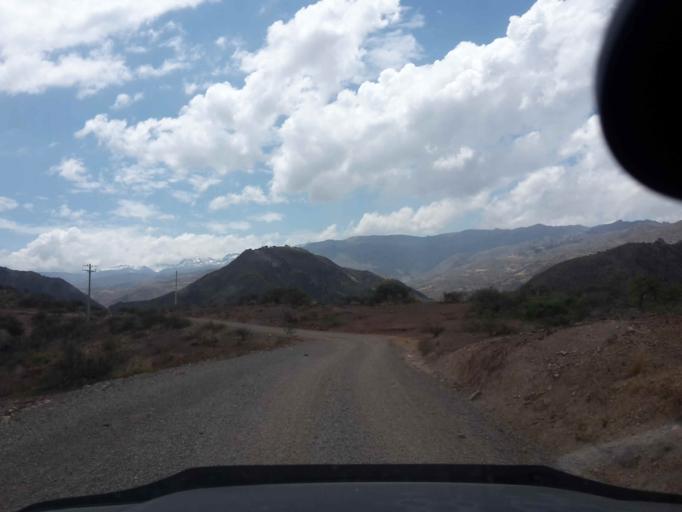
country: BO
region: Cochabamba
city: Sipe Sipe
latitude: -17.5386
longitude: -66.4853
